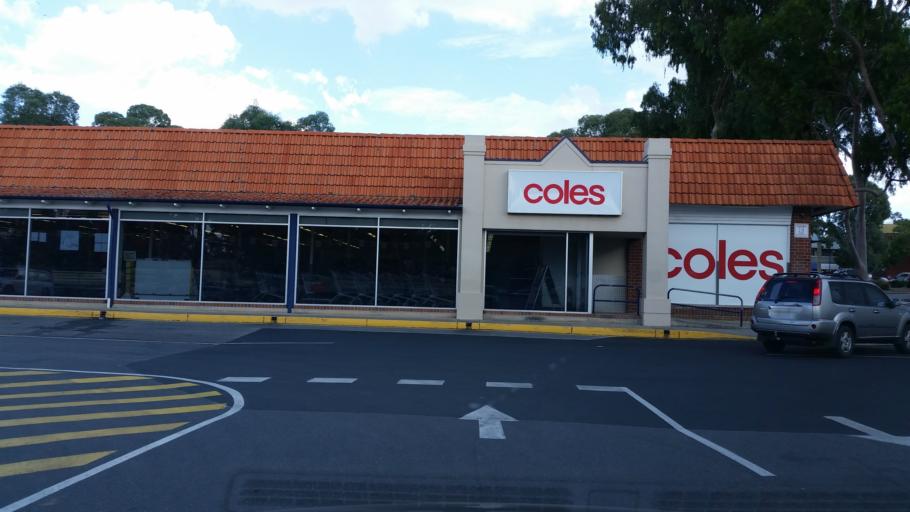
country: AU
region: South Australia
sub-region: Salisbury
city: Salisbury
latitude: -34.7607
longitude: 138.6477
